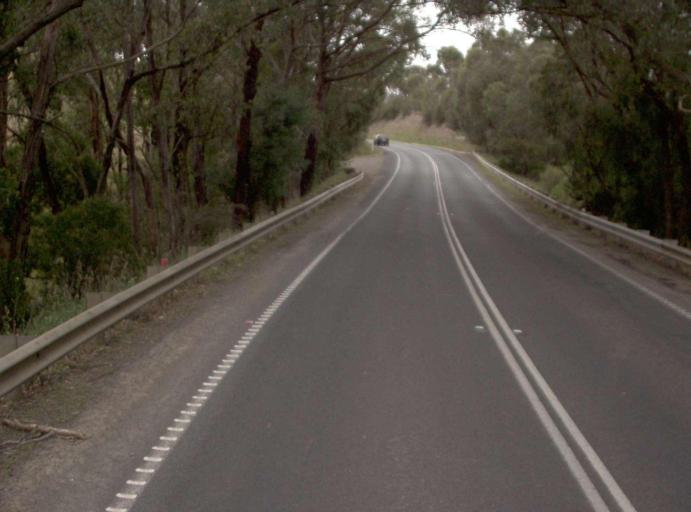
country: AU
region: Victoria
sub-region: Yarra Ranges
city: Yarra Glen
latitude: -37.5679
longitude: 145.4153
